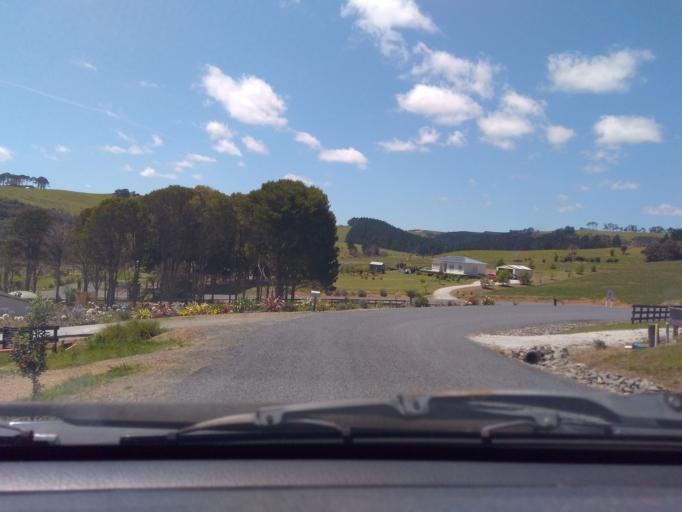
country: NZ
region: Northland
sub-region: Far North District
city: Taipa
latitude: -34.9965
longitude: 173.5119
